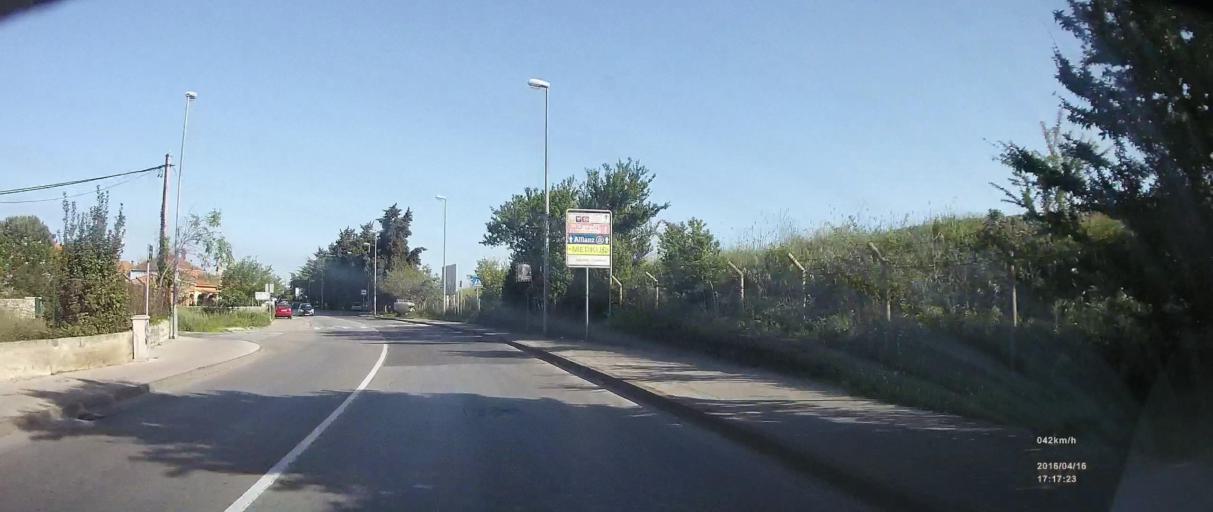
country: HR
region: Zadarska
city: Zadar
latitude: 44.1032
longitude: 15.2465
